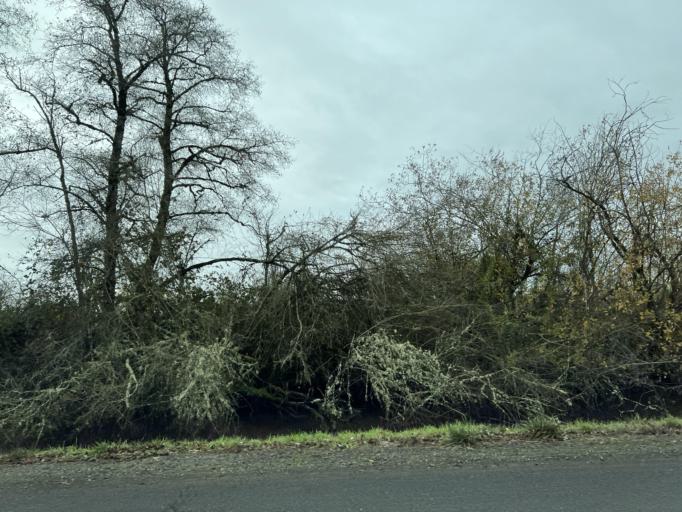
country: US
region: Oregon
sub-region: Marion County
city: Jefferson
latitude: 44.7986
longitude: -123.0864
